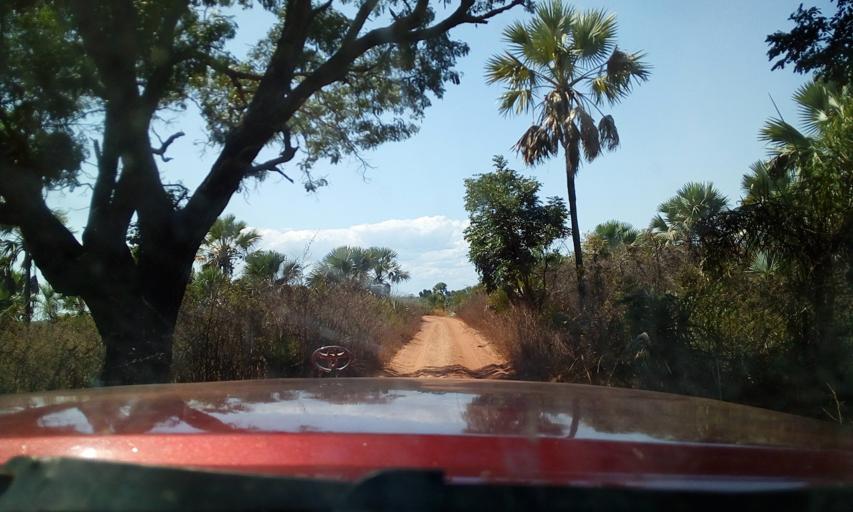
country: MG
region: Boeny
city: Sitampiky
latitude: -16.1258
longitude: 45.4325
